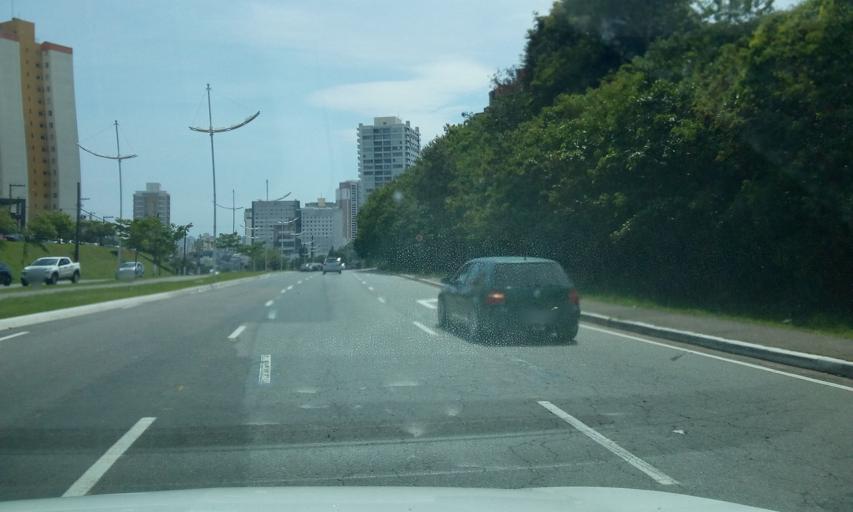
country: BR
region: Sao Paulo
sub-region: Jundiai
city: Jundiai
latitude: -23.2058
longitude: -46.8941
